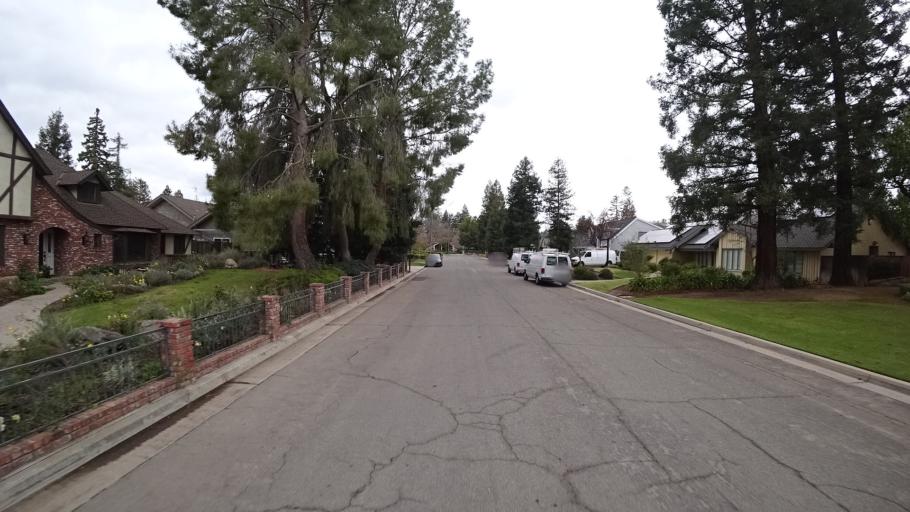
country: US
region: California
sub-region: Fresno County
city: Fresno
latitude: 36.8436
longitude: -119.8321
